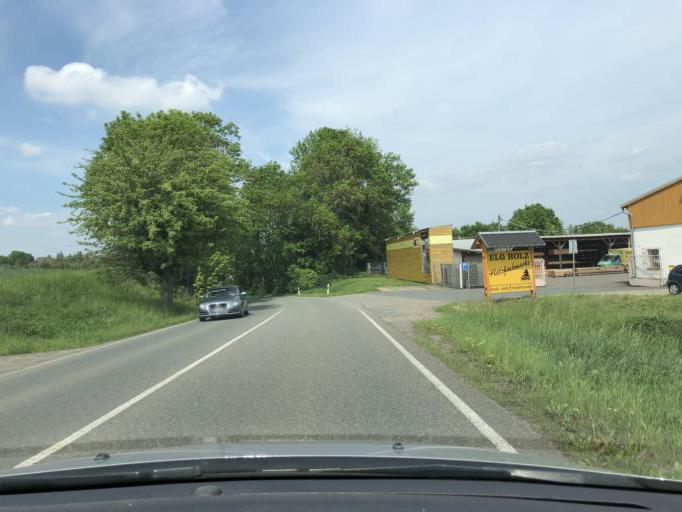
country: DE
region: Thuringia
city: Altenburg
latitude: 50.9707
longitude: 12.4179
